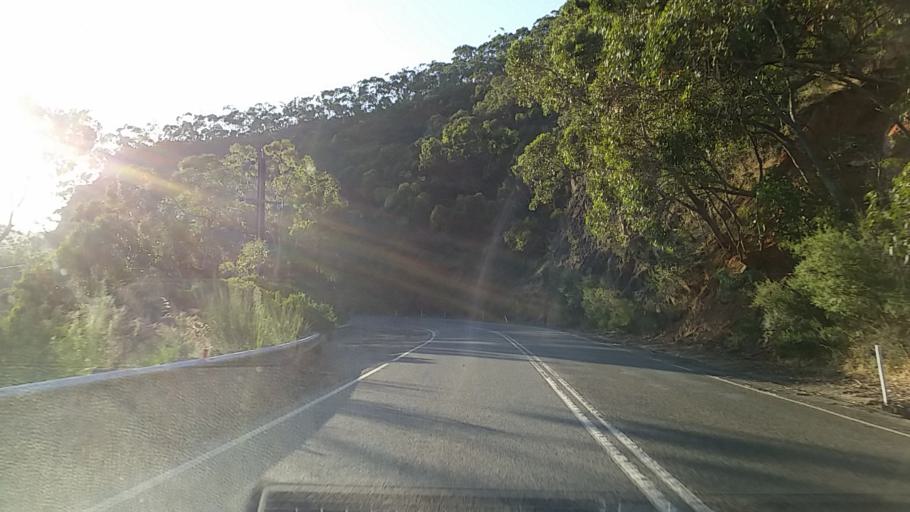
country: AU
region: South Australia
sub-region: Campbelltown
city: Athelstone
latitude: -34.8647
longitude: 138.7694
